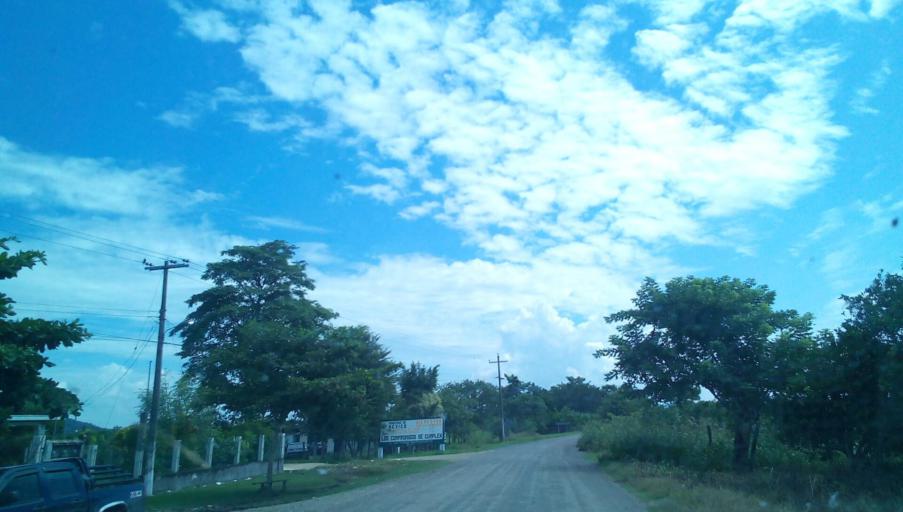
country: MX
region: Veracruz
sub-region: Alamo Temapache
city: Vegas de la Soledad y Soledad Dos
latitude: 20.9022
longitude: -97.9415
